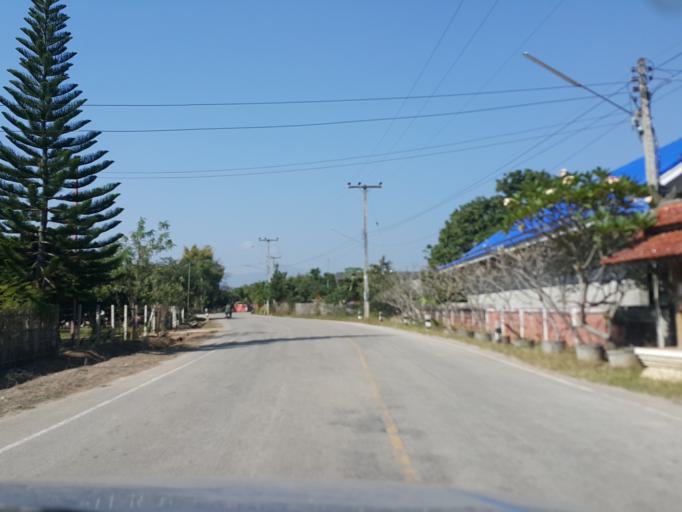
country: TH
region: Chiang Mai
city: Doi Lo
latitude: 18.5307
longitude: 98.7699
